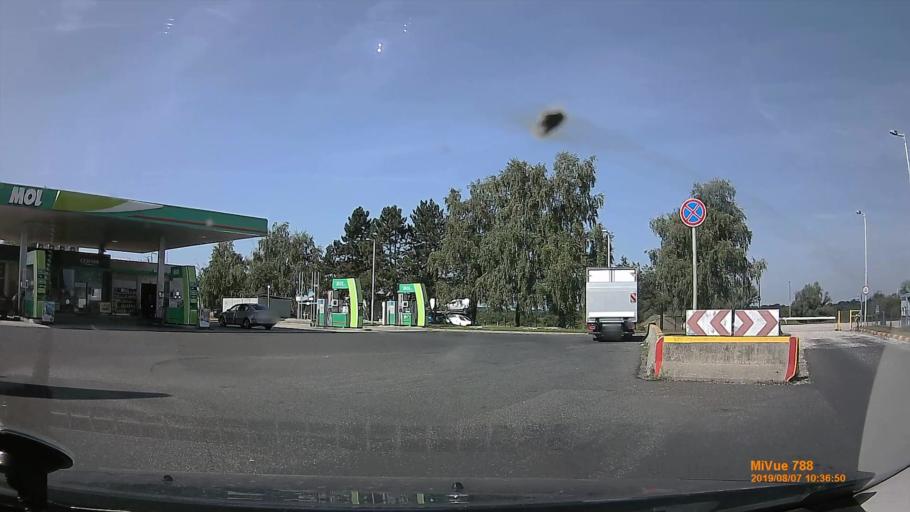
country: SI
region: Lendava-Lendva
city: Lendava
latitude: 46.6159
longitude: 16.4643
